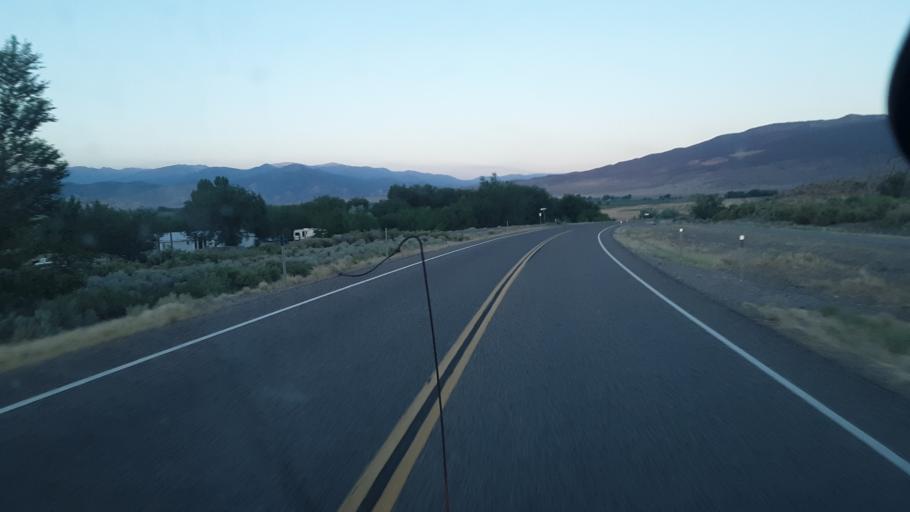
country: US
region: Utah
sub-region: Sevier County
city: Monroe
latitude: 38.6592
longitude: -112.1797
